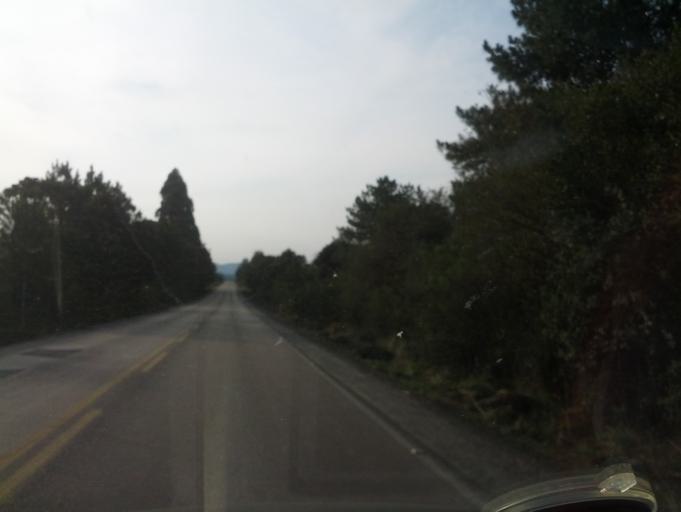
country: BR
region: Santa Catarina
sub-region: Otacilio Costa
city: Otacilio Costa
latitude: -27.4145
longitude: -50.1246
